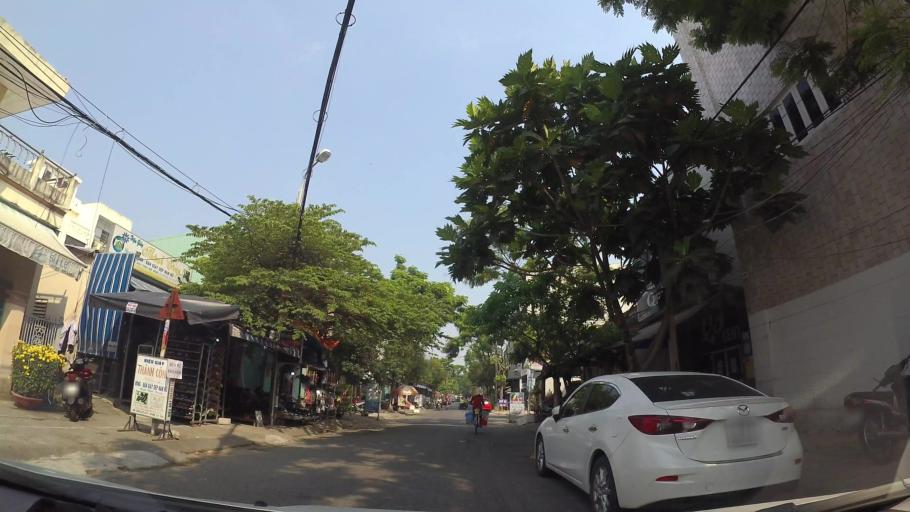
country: VN
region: Da Nang
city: Son Tra
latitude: 16.0407
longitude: 108.2427
